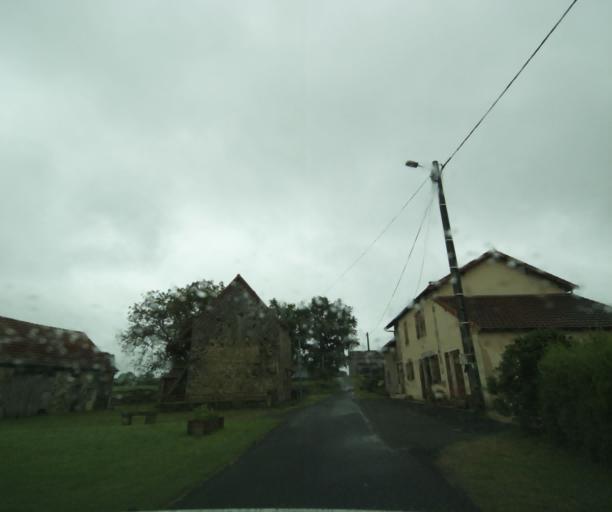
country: FR
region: Bourgogne
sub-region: Departement de Saone-et-Loire
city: Ciry-le-Noble
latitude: 46.5363
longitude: 4.3681
